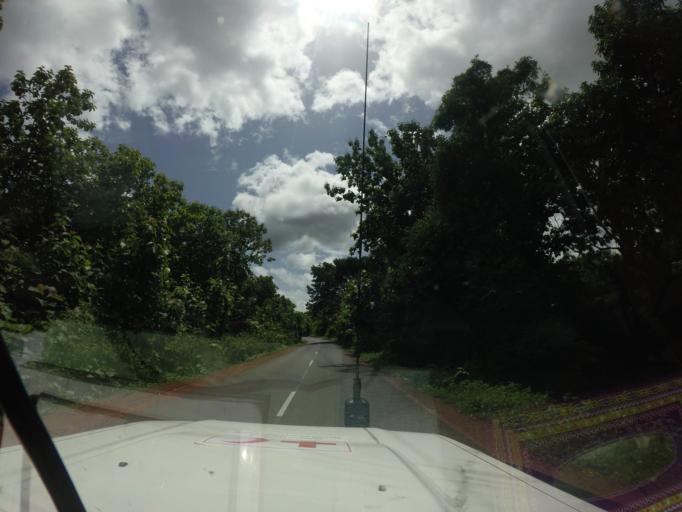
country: SL
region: Northern Province
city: Bindi
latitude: 10.1730
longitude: -11.7132
